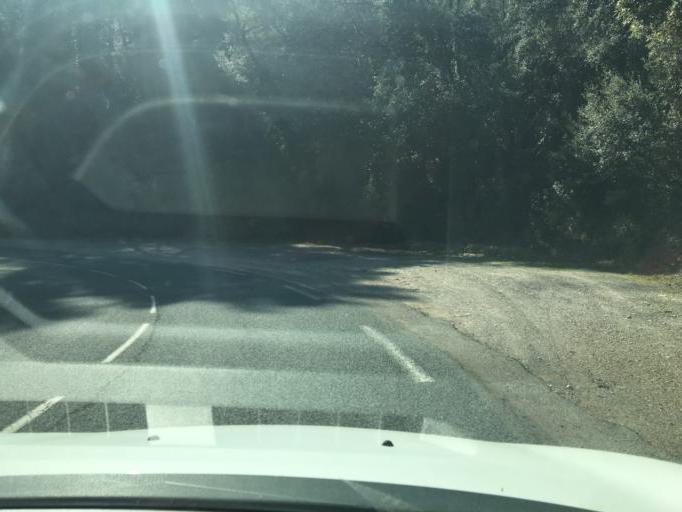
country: FR
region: Provence-Alpes-Cote d'Azur
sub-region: Departement du Var
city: Bargemon
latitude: 43.6030
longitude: 6.5498
